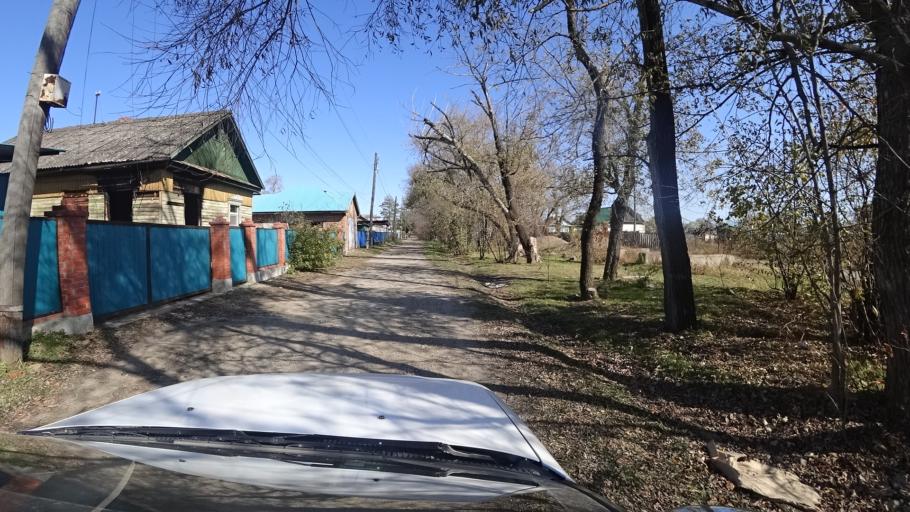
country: RU
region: Primorskiy
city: Dal'nerechensk
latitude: 45.9288
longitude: 133.7390
